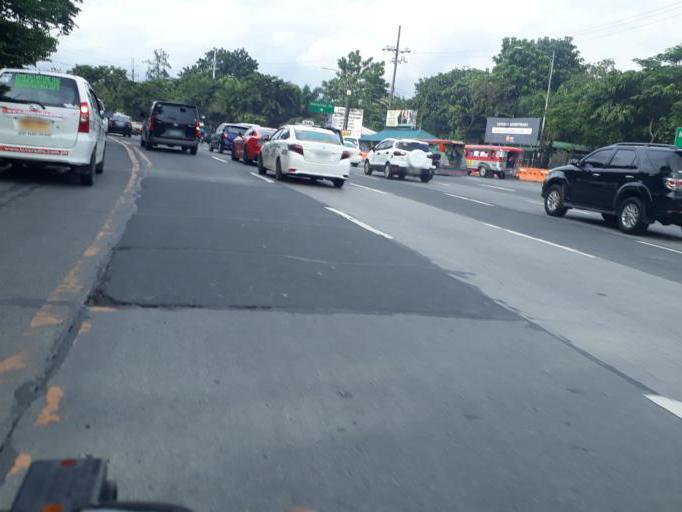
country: PH
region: Metro Manila
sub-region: Quezon City
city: Quezon City
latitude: 14.6498
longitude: 121.0515
